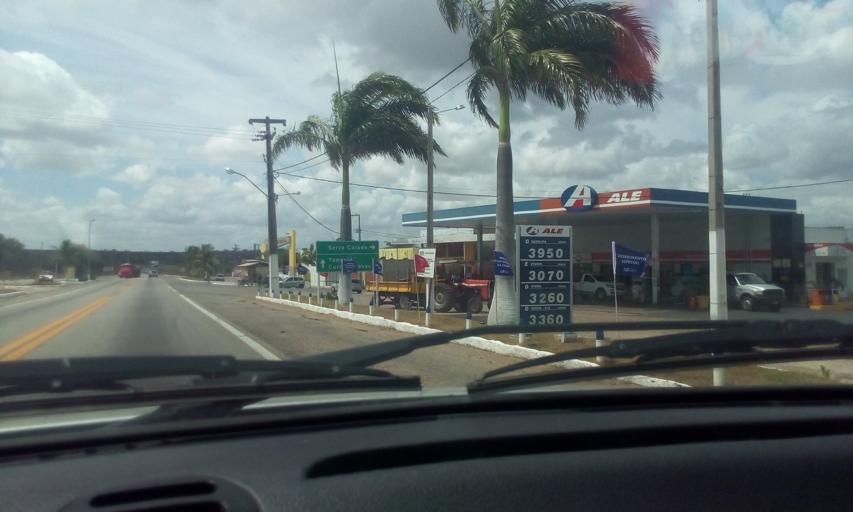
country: BR
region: Rio Grande do Norte
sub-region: Tangara
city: Tangara
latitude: -6.1067
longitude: -35.7086
